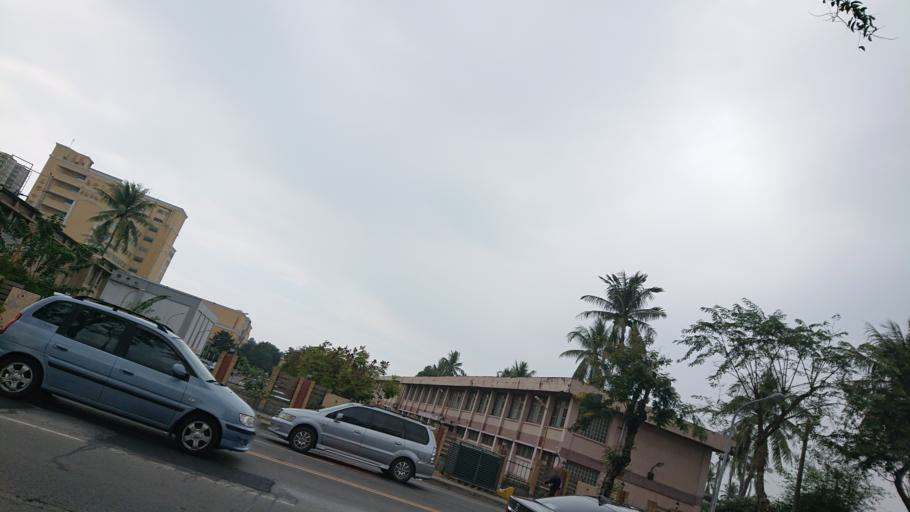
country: TW
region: Kaohsiung
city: Kaohsiung
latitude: 22.7023
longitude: 120.2926
